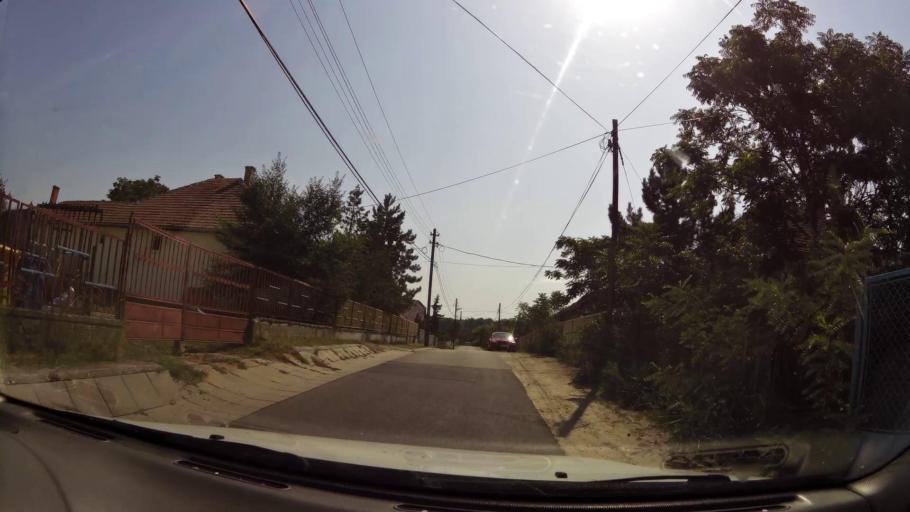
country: HU
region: Pest
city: Ujszilvas
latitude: 47.2713
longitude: 19.9130
